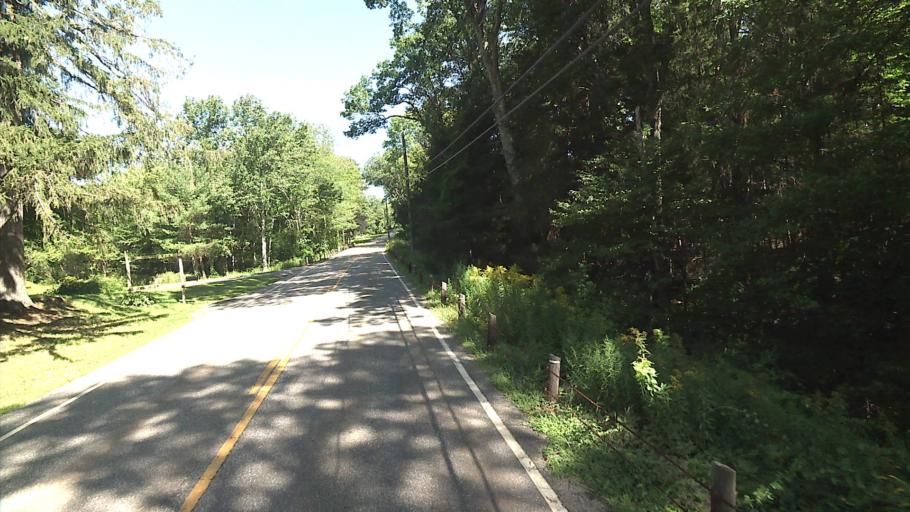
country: US
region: Connecticut
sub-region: Litchfield County
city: Northwest Harwinton
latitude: 41.7458
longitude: -73.0793
